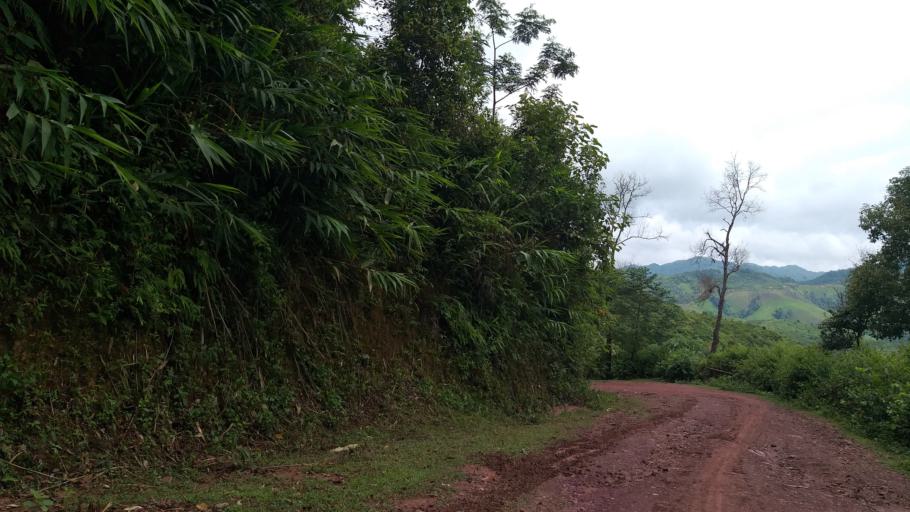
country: LA
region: Phongsali
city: Khoa
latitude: 21.3782
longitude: 102.6339
